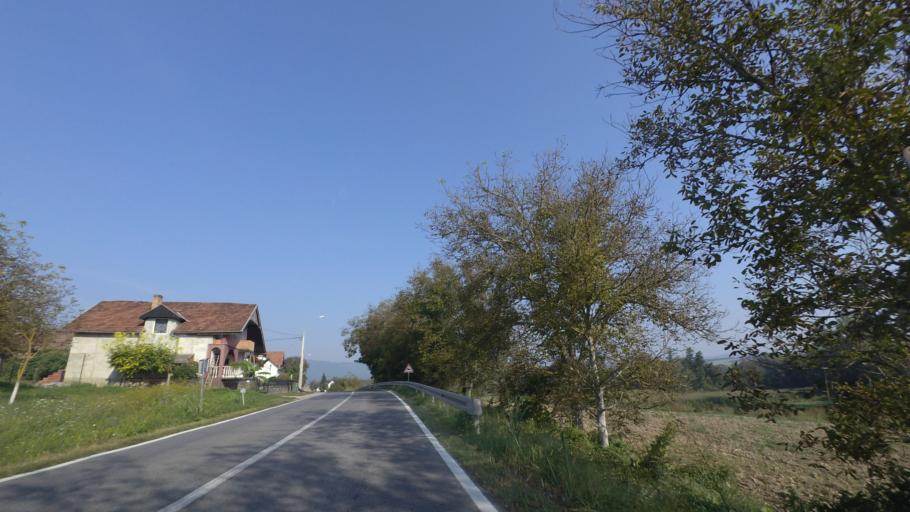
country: HR
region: Pozesko-Slavonska
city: Pozega
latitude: 45.3531
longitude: 17.5556
